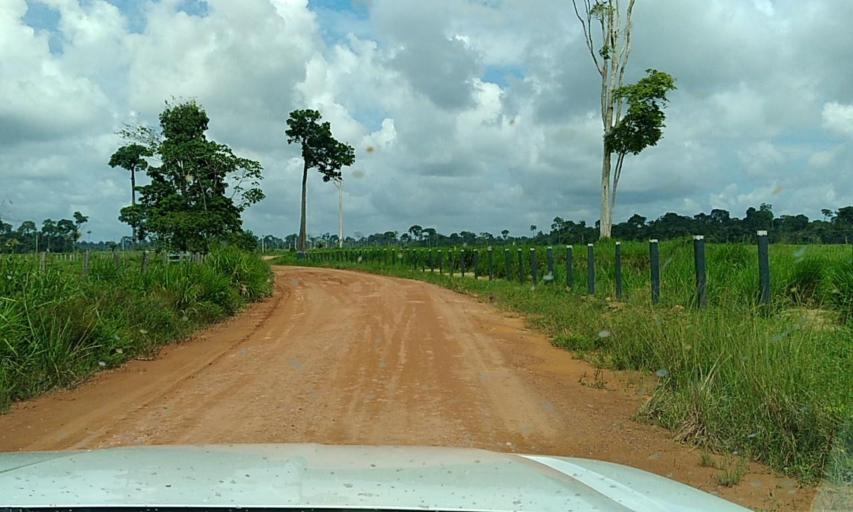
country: BR
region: Para
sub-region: Senador Jose Porfirio
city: Senador Jose Porfirio
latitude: -2.5179
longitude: -51.8485
